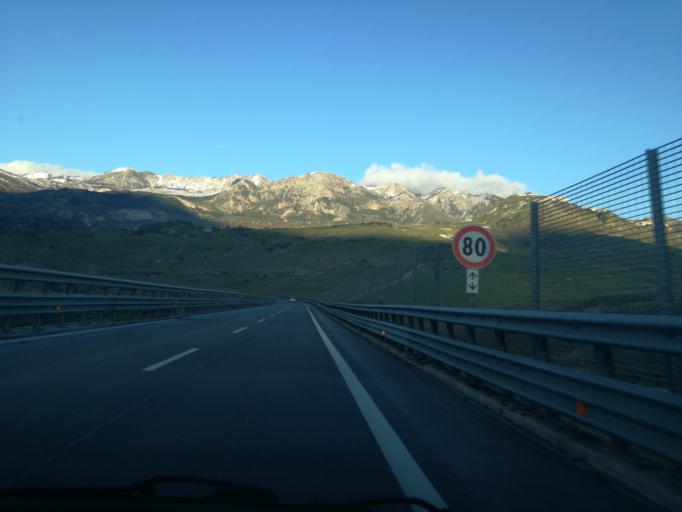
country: IT
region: Sicily
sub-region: Palermo
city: Polizzi Generosa
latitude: 37.8060
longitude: 13.9697
